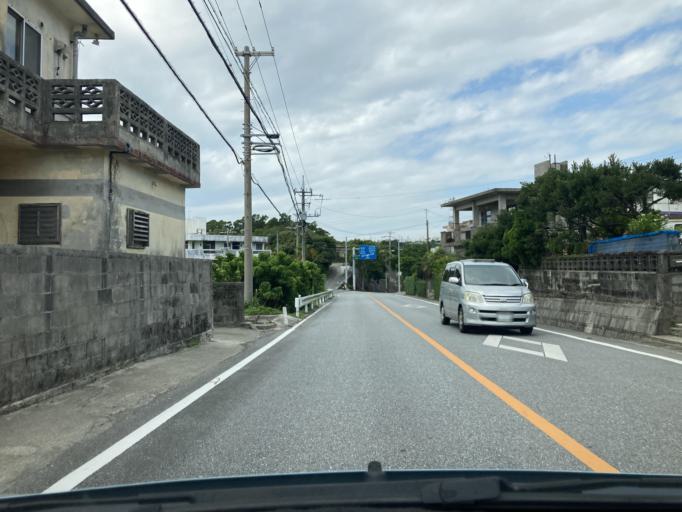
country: JP
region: Okinawa
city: Ginowan
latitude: 26.2702
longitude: 127.7818
